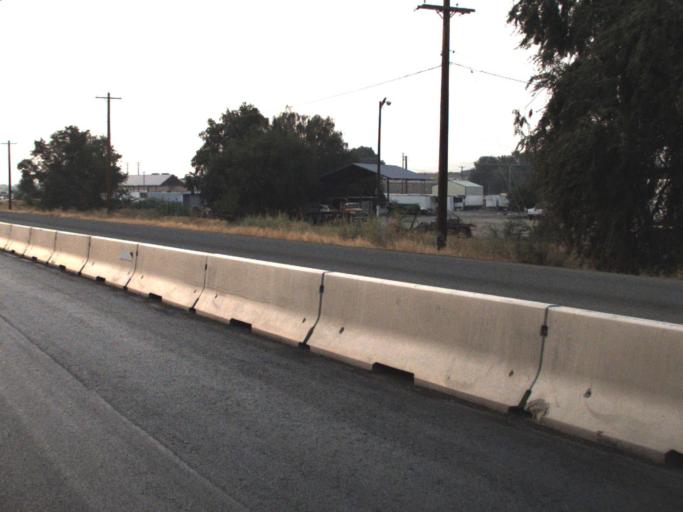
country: US
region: Washington
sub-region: Yakima County
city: Toppenish
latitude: 46.3779
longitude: -120.3354
